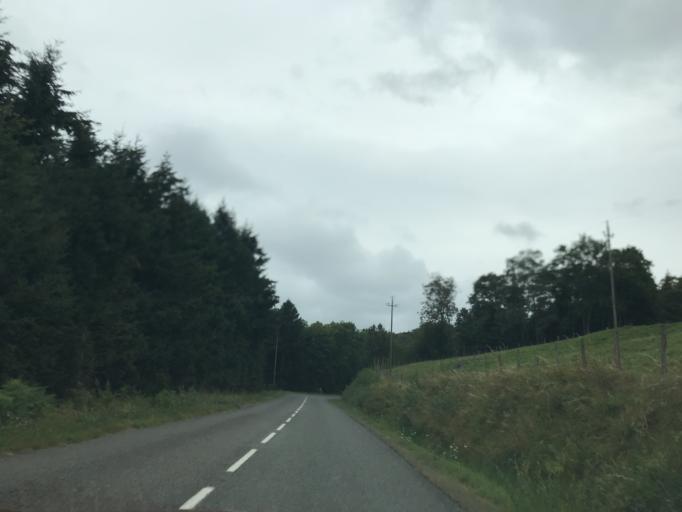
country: FR
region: Rhone-Alpes
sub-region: Departement de la Loire
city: Sail-sous-Couzan
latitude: 45.6795
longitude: 3.8747
